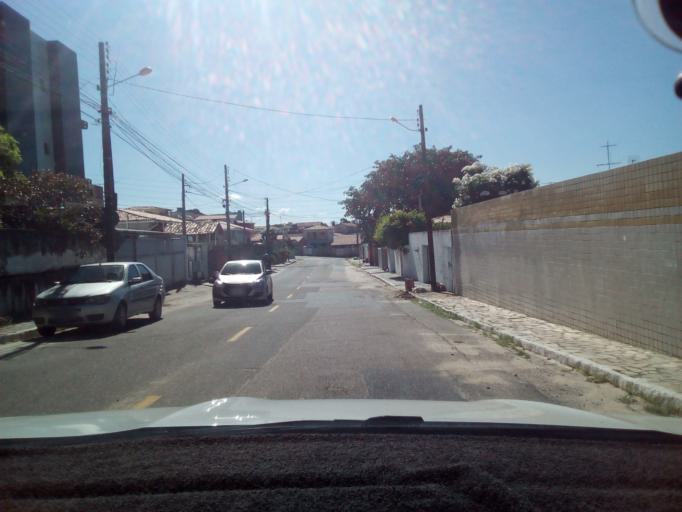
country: BR
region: Paraiba
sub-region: Joao Pessoa
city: Joao Pessoa
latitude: -7.1075
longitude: -34.8669
